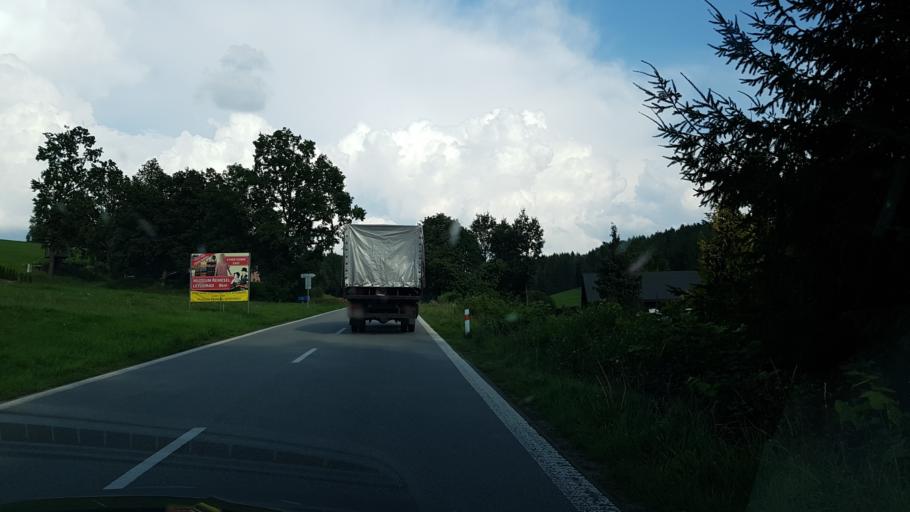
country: CZ
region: Pardubicky
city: Jablonne nad Orlici
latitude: 50.0946
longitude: 16.5690
